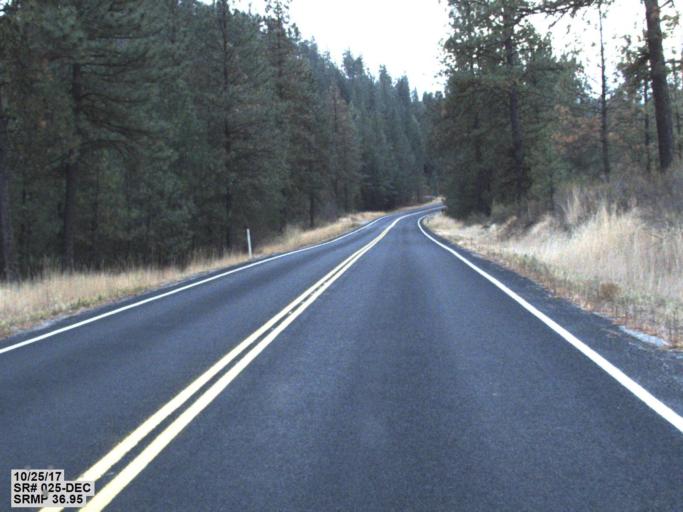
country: US
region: Washington
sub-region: Lincoln County
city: Davenport
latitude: 48.0602
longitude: -118.2163
